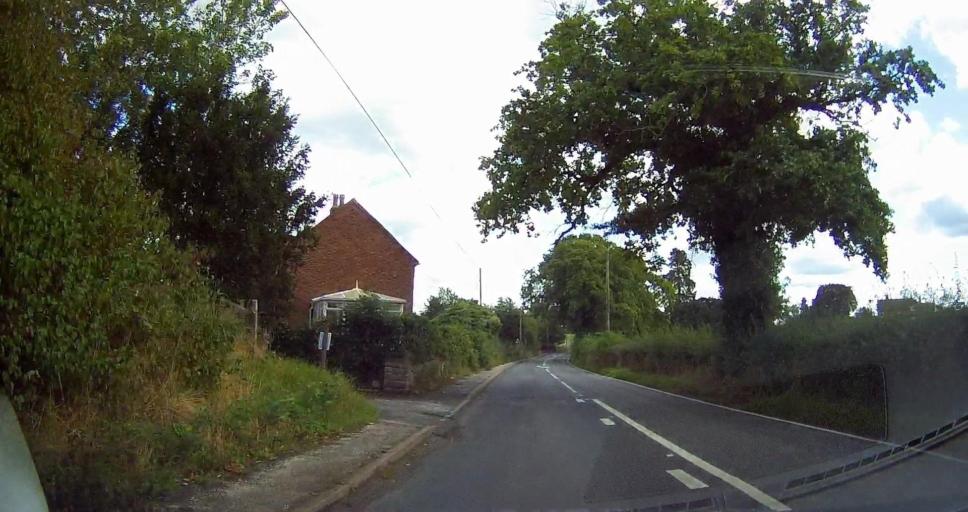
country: GB
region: England
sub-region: Shropshire
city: Market Drayton
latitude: 52.9852
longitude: -2.4784
